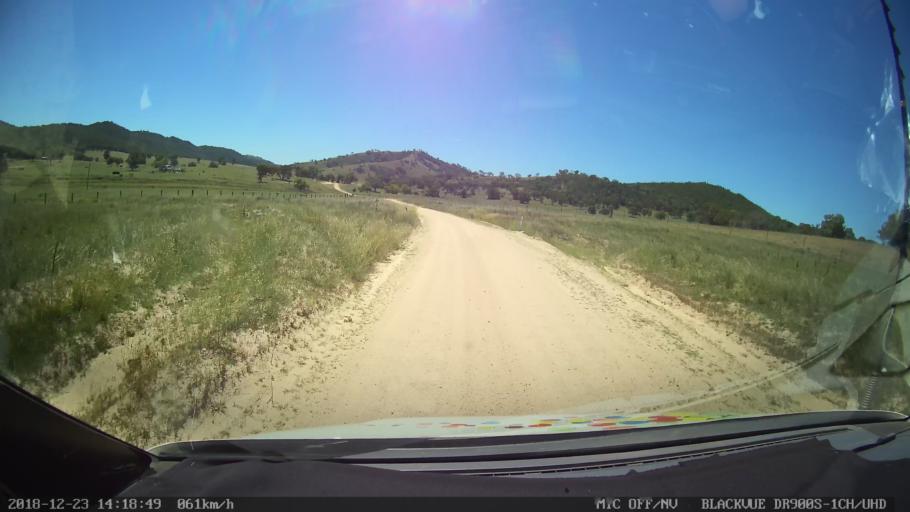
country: AU
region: New South Wales
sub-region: Tamworth Municipality
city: Manilla
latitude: -30.6560
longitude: 151.0005
